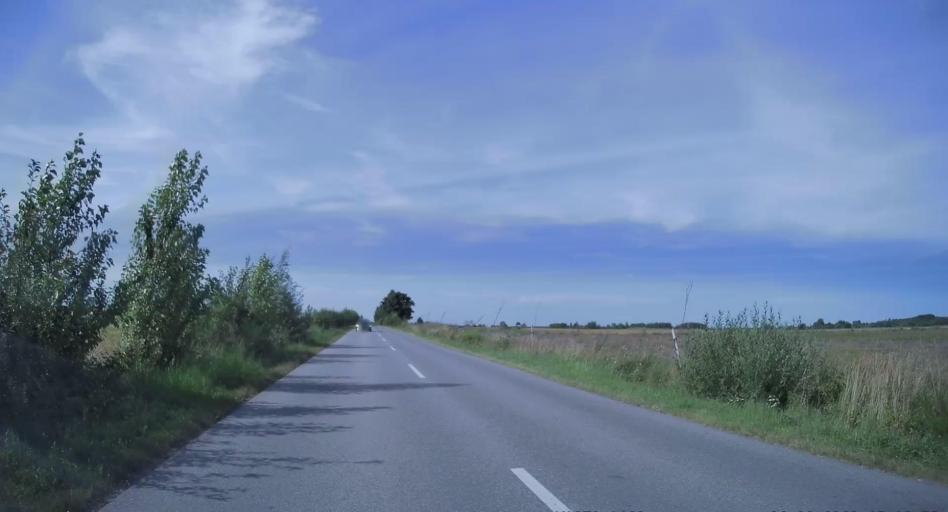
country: PL
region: Lodz Voivodeship
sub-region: Powiat opoczynski
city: Mniszkow
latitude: 51.3790
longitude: 20.0367
